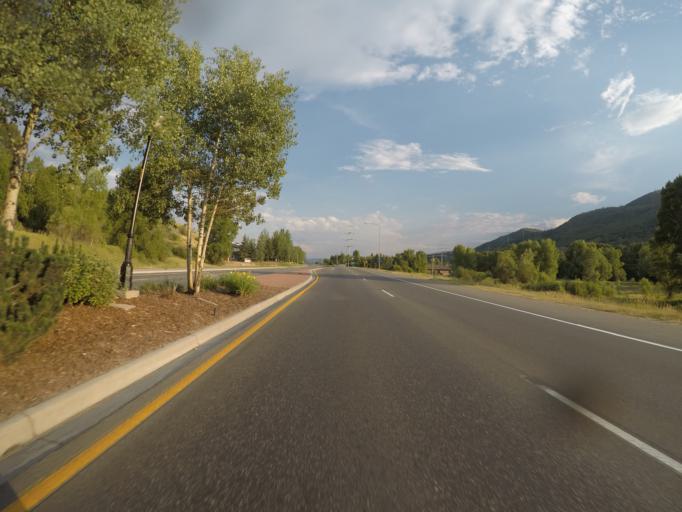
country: US
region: Colorado
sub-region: Routt County
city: Steamboat Springs
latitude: 40.4708
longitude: -106.8264
